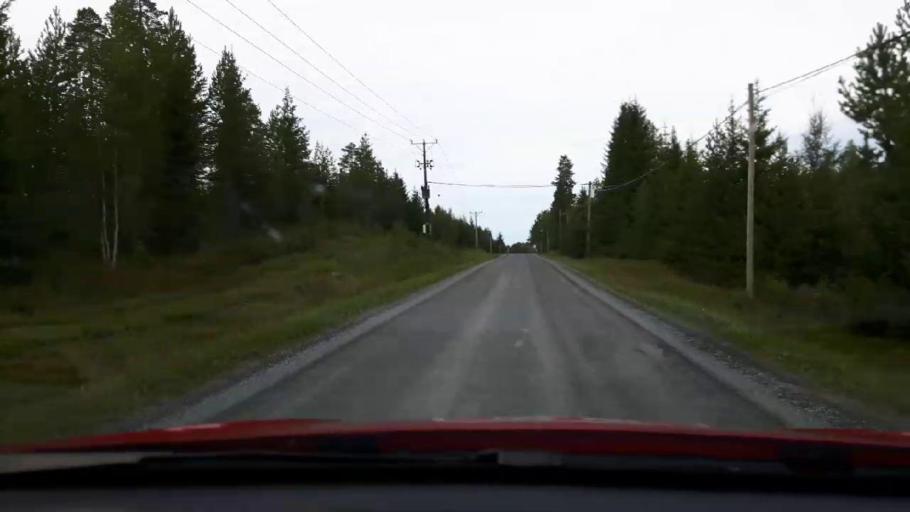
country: SE
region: Jaemtland
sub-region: Krokoms Kommun
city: Valla
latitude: 63.2498
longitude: 13.9583
